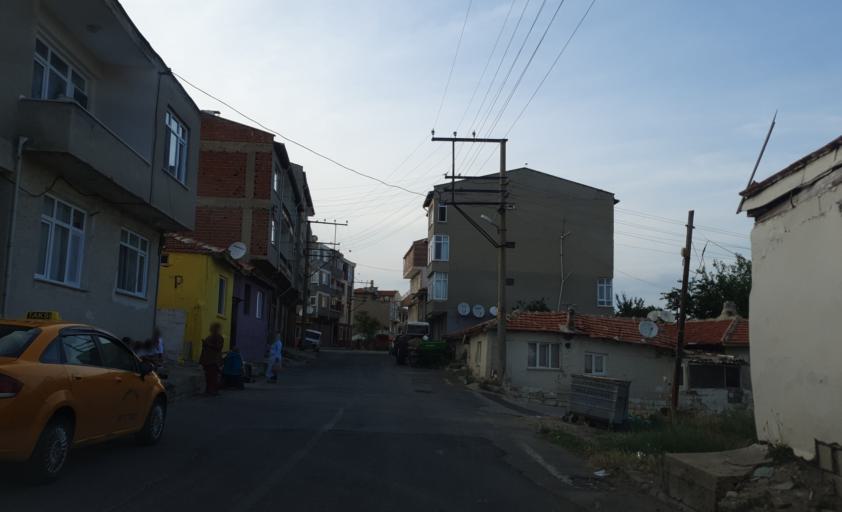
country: TR
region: Tekirdag
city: Hayrabolu
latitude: 41.2156
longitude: 27.1095
